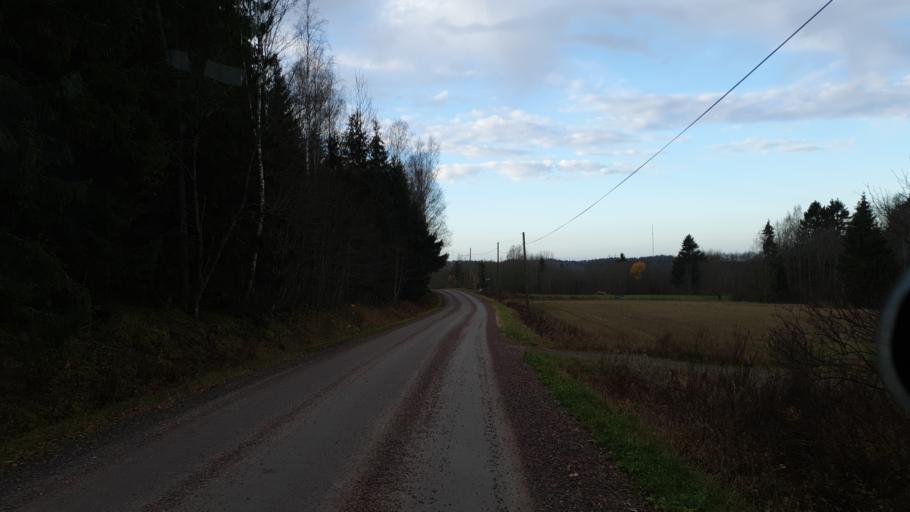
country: FI
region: Uusimaa
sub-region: Helsinki
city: Siuntio
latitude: 60.1459
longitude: 24.2658
